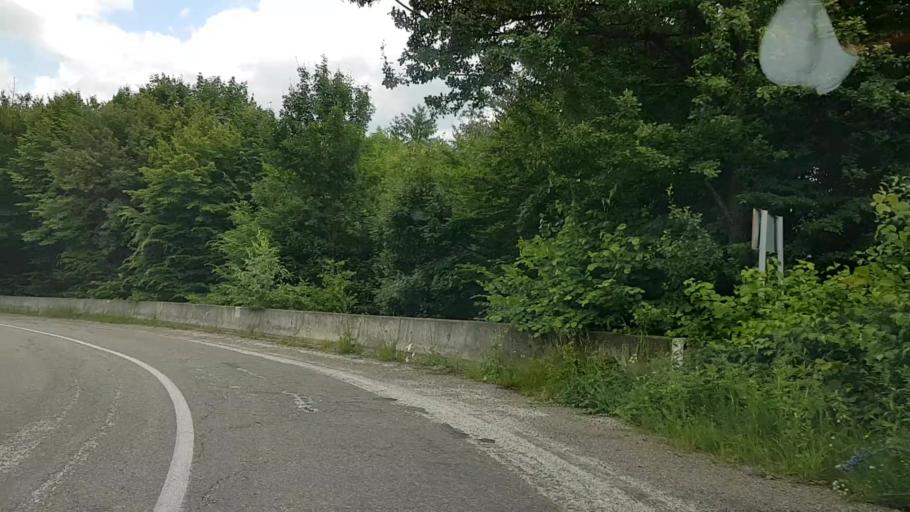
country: RO
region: Neamt
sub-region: Comuna Pangarati
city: Pangarati
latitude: 46.9549
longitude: 26.1227
